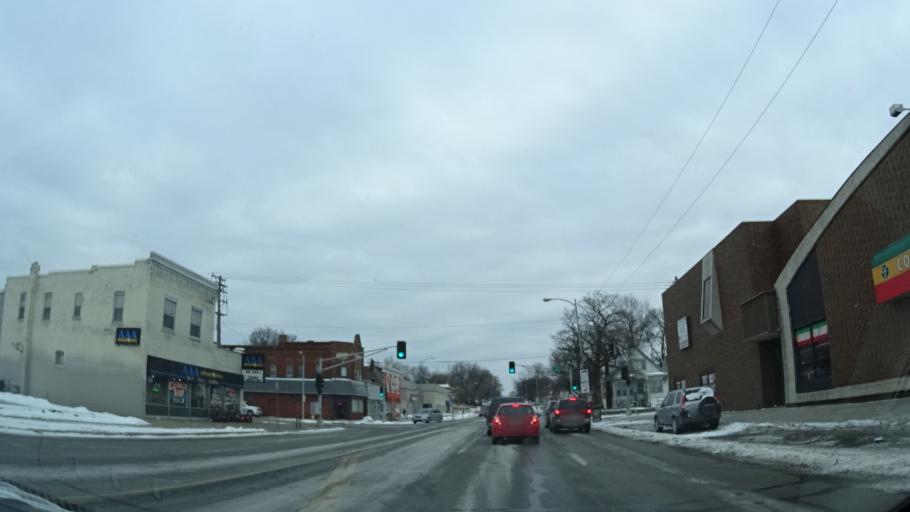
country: US
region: Nebraska
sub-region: Douglas County
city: Omaha
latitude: 41.2192
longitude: -95.9470
